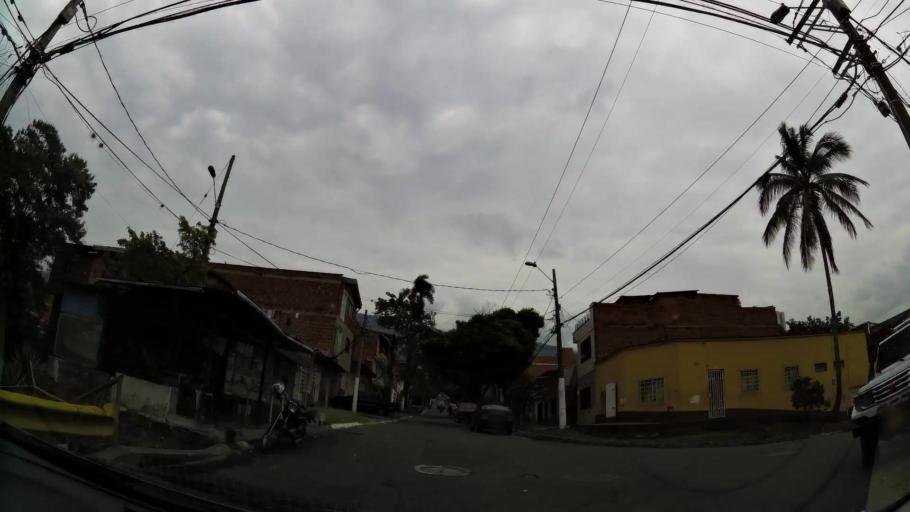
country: CO
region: Antioquia
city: Medellin
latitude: 6.2712
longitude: -75.5606
